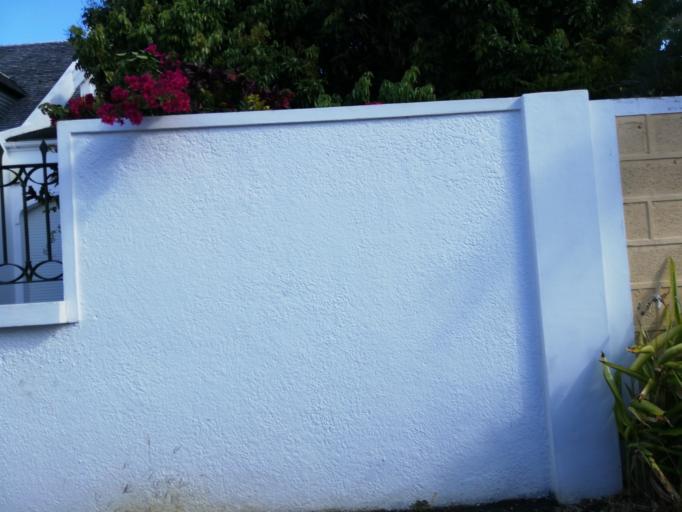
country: MU
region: Moka
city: Moka
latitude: -20.2233
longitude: 57.4764
